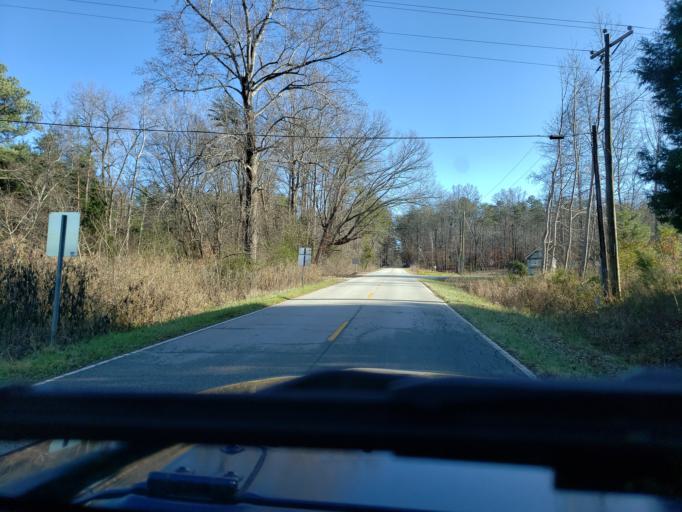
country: US
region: North Carolina
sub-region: Cleveland County
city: White Plains
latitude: 35.1540
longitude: -81.3973
